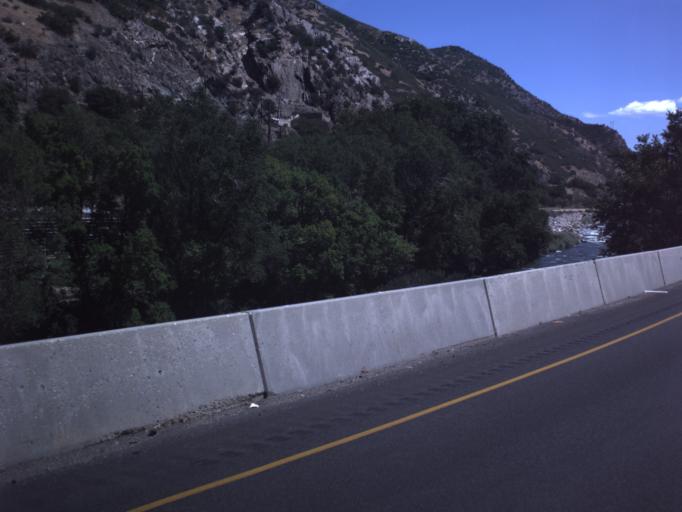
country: US
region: Utah
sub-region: Weber County
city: Uintah
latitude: 41.1370
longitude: -111.8845
